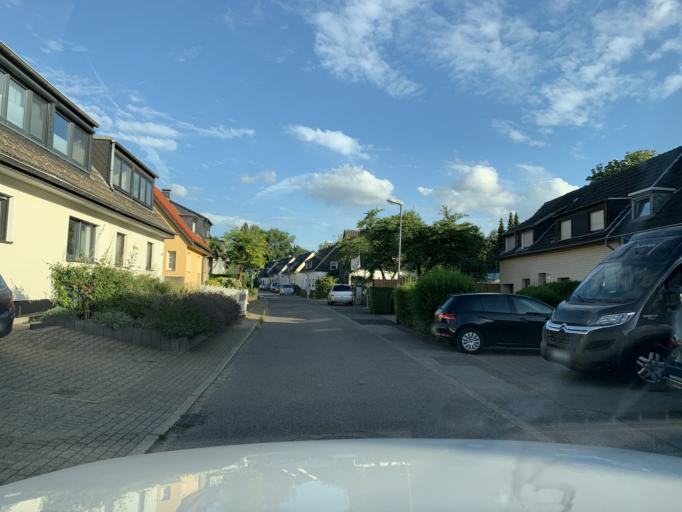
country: DE
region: North Rhine-Westphalia
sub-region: Regierungsbezirk Dusseldorf
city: Oberhausen
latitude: 51.4637
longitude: 6.9187
